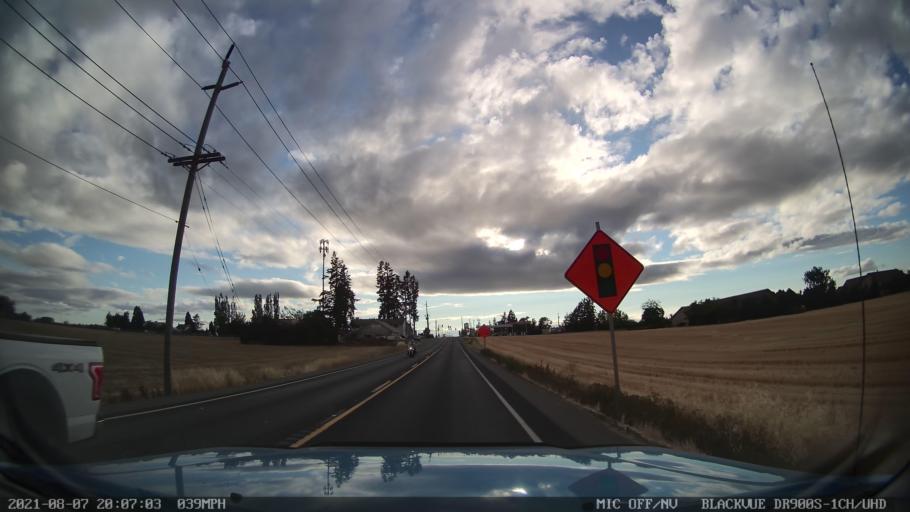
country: US
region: Oregon
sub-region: Marion County
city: Silverton
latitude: 44.9914
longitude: -122.8768
